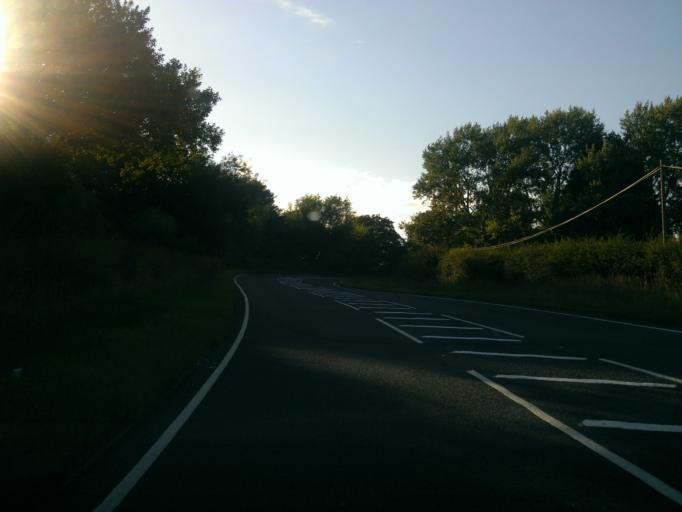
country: GB
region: England
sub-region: Essex
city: Alresford
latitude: 51.8500
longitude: 1.0132
